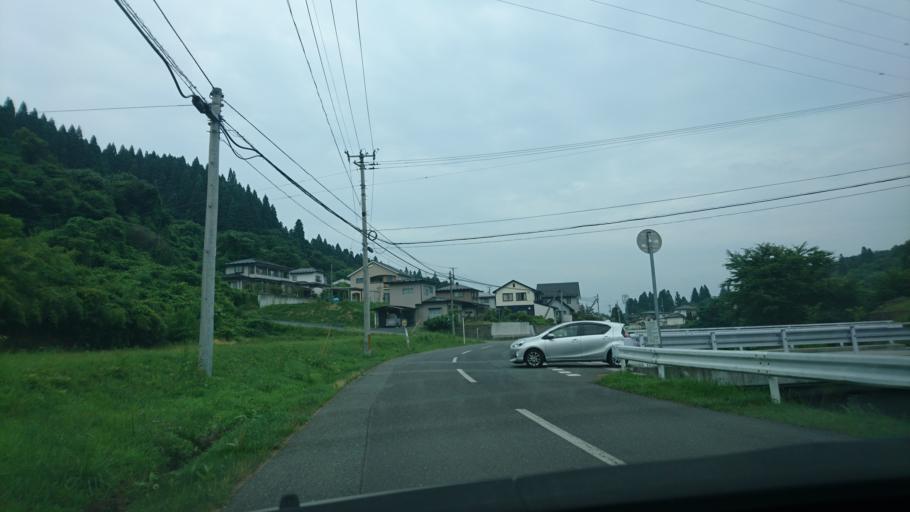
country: JP
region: Iwate
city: Ichinoseki
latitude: 38.9083
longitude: 141.1194
